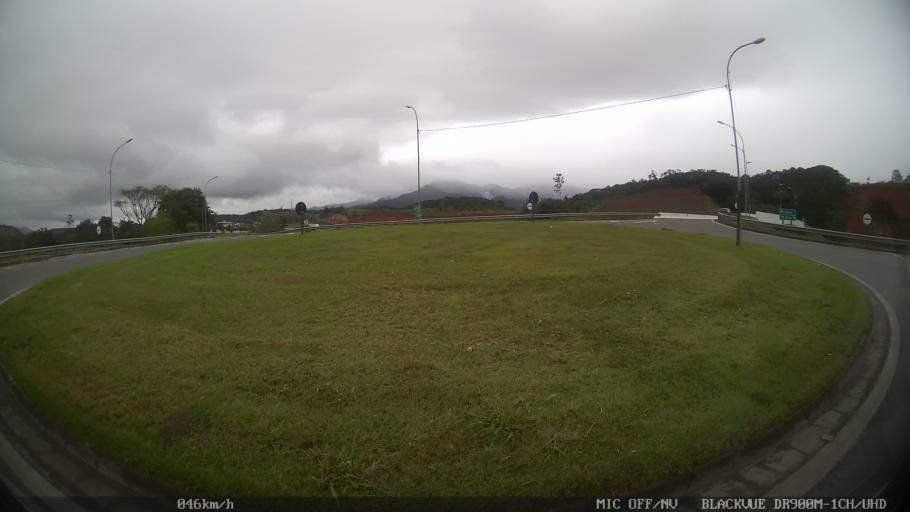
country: BR
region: Sao Paulo
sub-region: Juquia
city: Juquia
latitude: -24.3308
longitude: -47.6350
